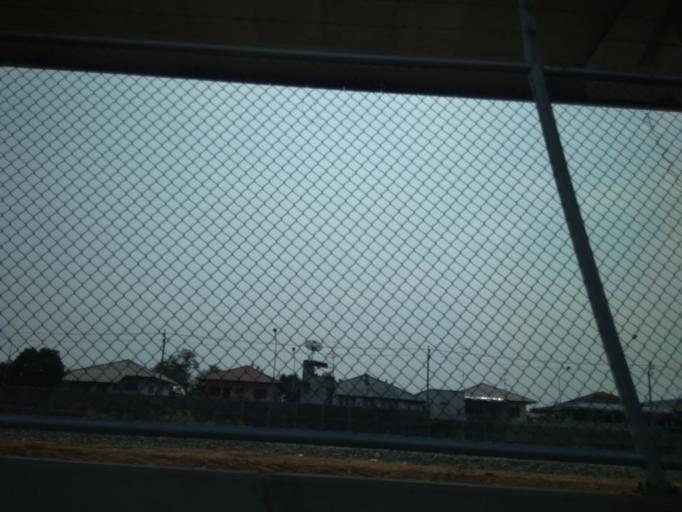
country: TH
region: Bangkok
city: Taling Chan
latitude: 13.7947
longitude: 100.4336
